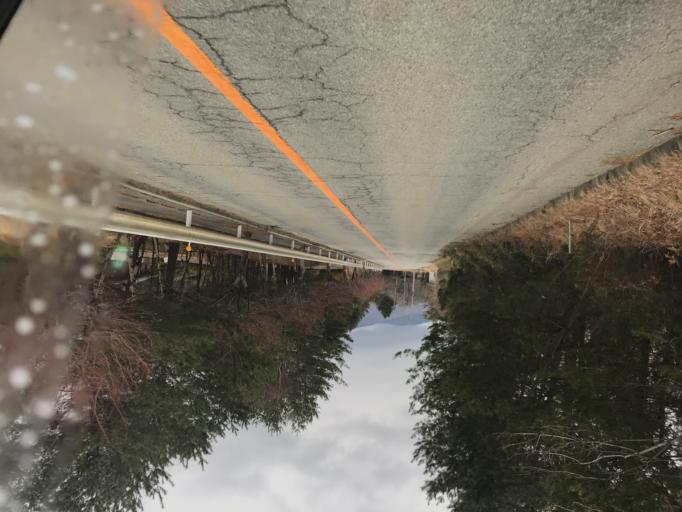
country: JP
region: Nagano
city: Chino
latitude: 35.8839
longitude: 138.3188
